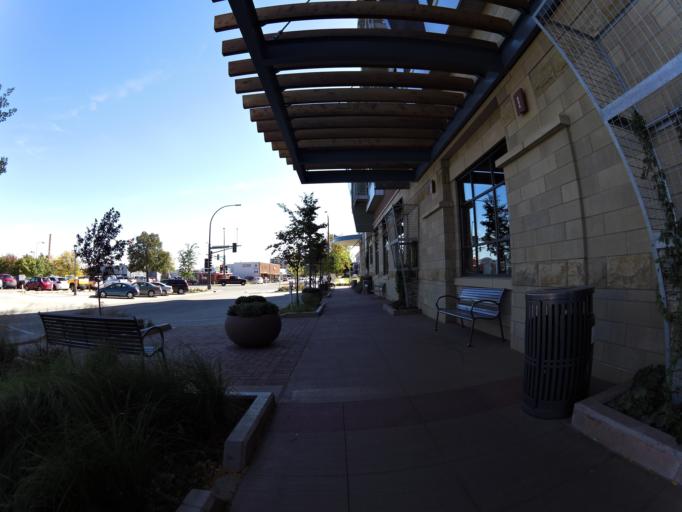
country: US
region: Minnesota
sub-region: Olmsted County
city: Rochester
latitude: 44.0415
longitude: -92.4217
